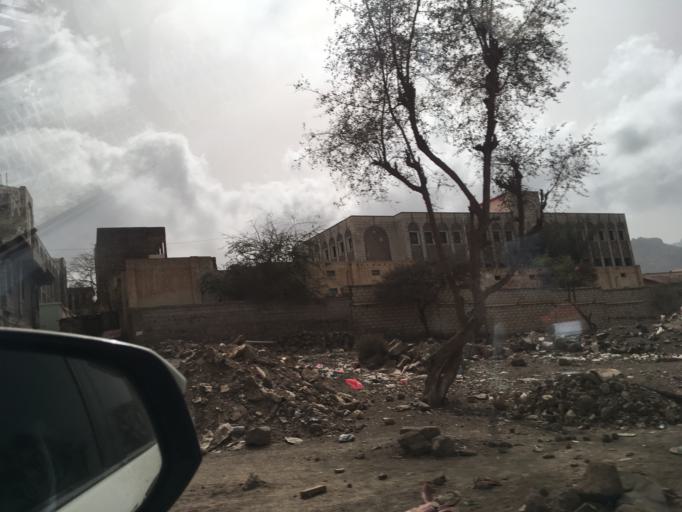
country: YE
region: Ad Dali'
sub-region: Ad Dhale'e
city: Dhalie
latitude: 13.7057
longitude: 44.7357
